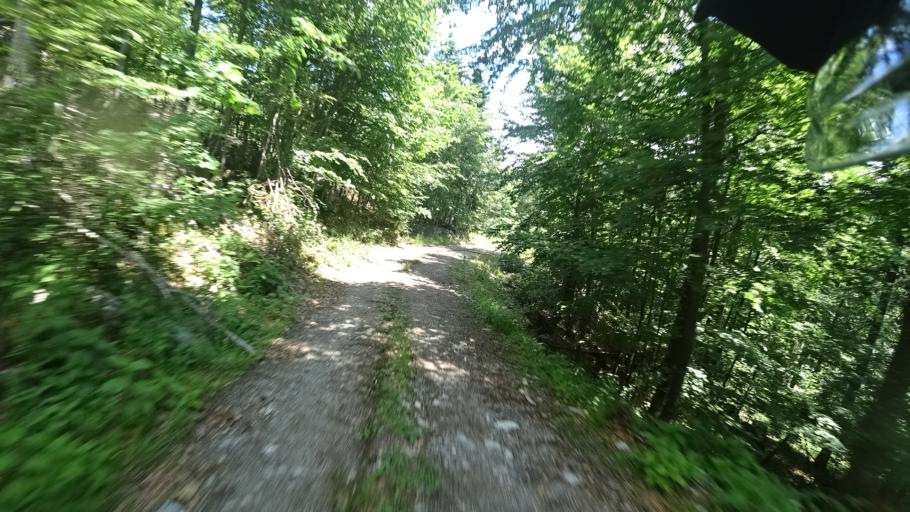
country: SI
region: Osilnica
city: Osilnica
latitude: 45.4890
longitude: 14.7175
